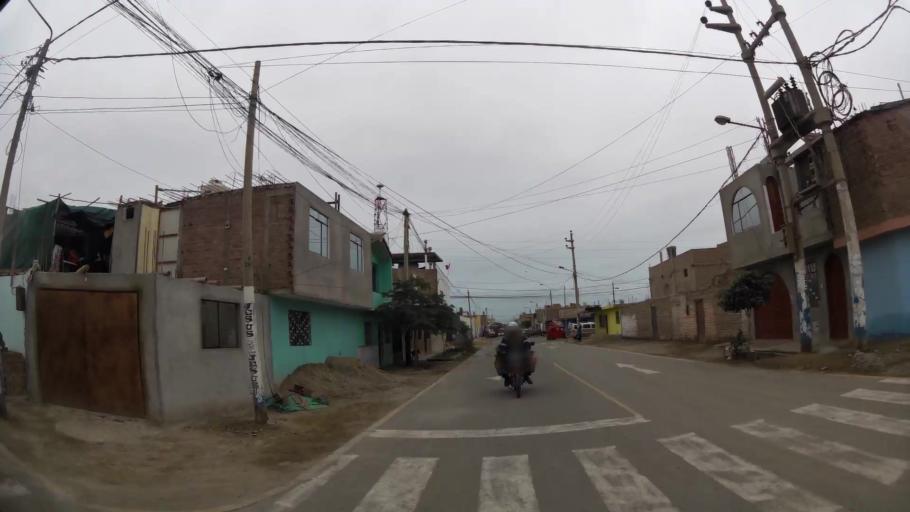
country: PE
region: Ica
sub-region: Provincia de Pisco
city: Pisco
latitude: -13.7164
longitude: -76.1986
